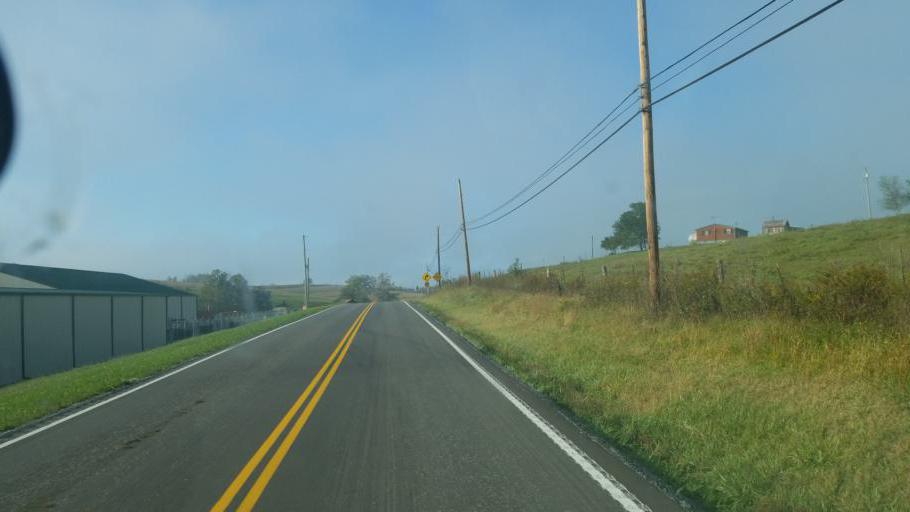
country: US
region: Kentucky
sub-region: Fleming County
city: Flemingsburg
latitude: 38.4544
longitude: -83.6820
